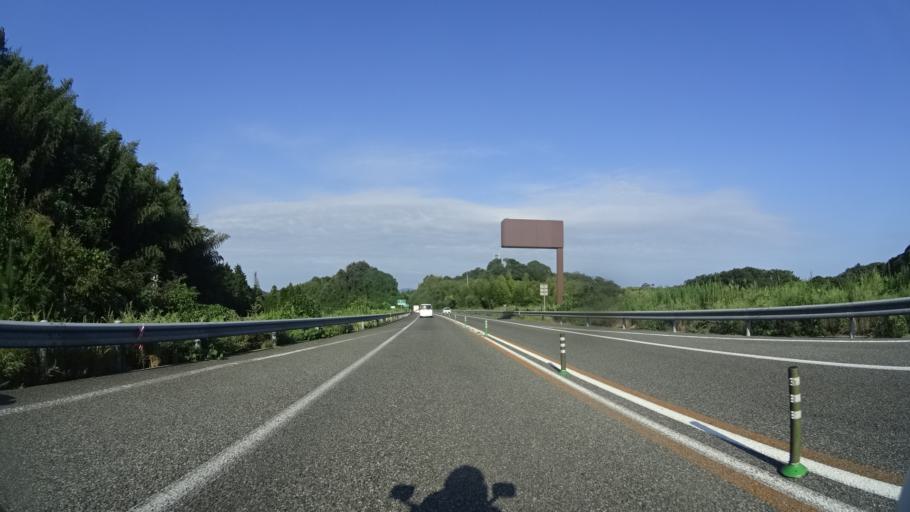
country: JP
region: Shimane
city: Matsue-shi
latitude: 35.4118
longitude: 132.9599
